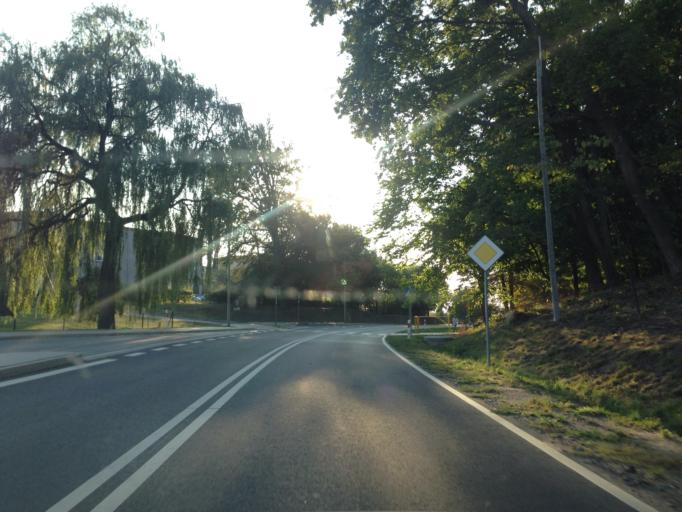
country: PL
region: Warmian-Masurian Voivodeship
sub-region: Powiat ilawski
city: Susz
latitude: 53.6979
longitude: 19.3846
